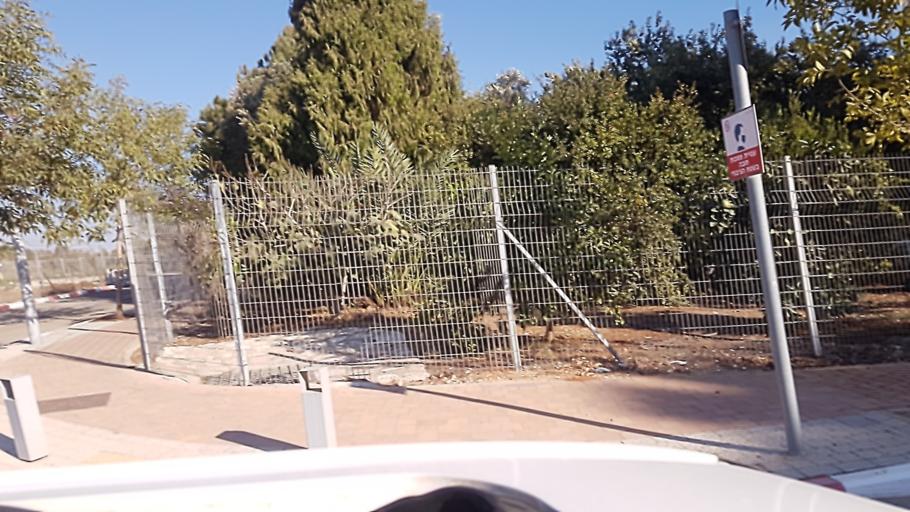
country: IL
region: Central District
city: Kfar Saba
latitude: 32.2032
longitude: 34.9283
